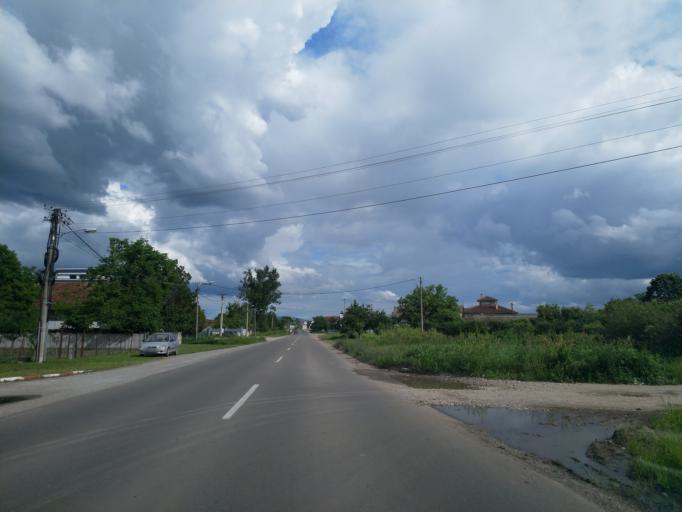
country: RS
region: Central Serbia
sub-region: Pomoravski Okrug
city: Paracin
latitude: 43.8758
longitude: 21.3953
